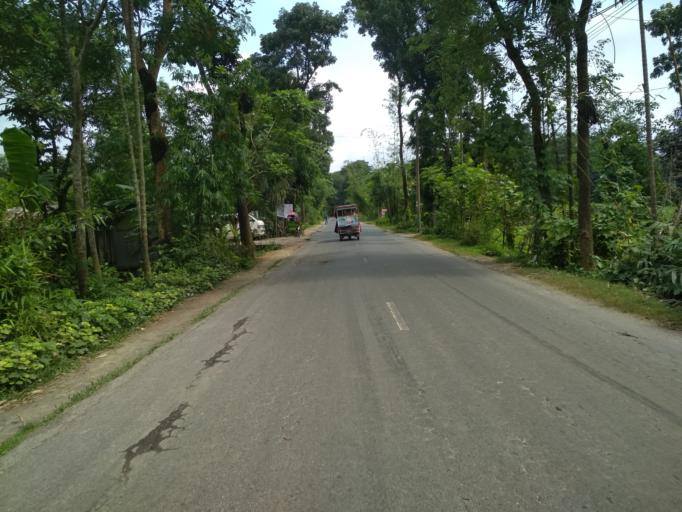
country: BD
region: Chittagong
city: Lakshmipur
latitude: 22.9537
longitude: 90.8089
